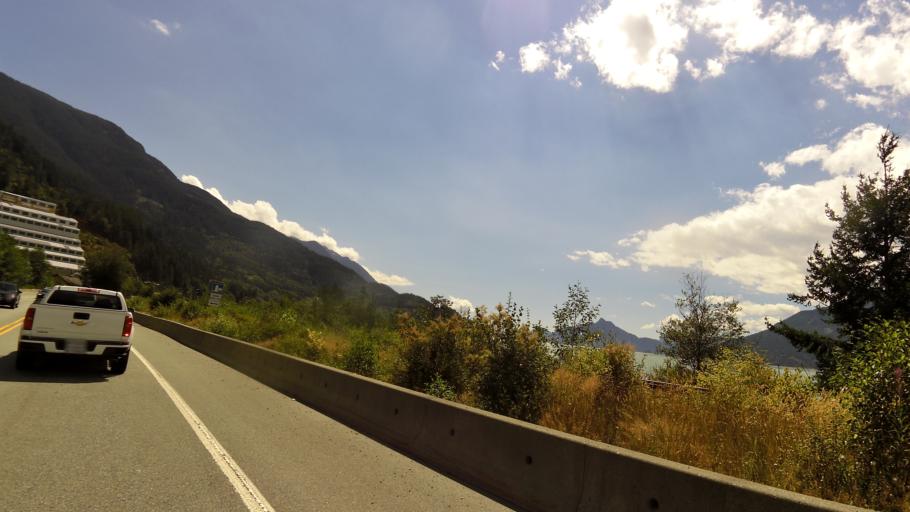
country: CA
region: British Columbia
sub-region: Greater Vancouver Regional District
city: Lions Bay
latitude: 49.6268
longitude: -123.2071
